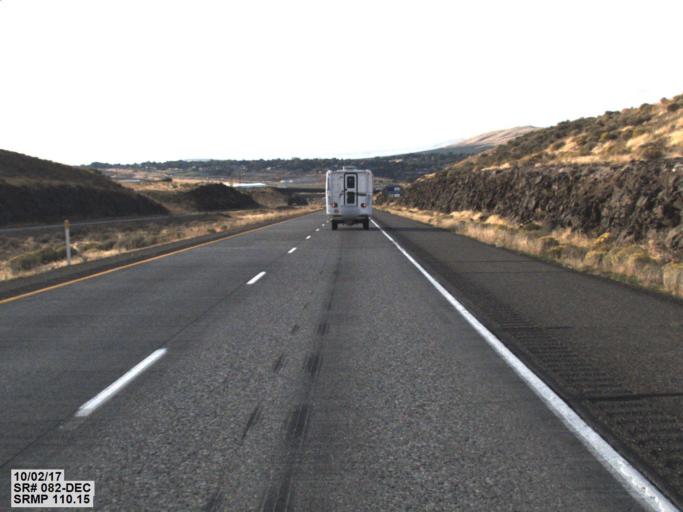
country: US
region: Washington
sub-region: Franklin County
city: West Pasco
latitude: 46.1845
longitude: -119.2480
